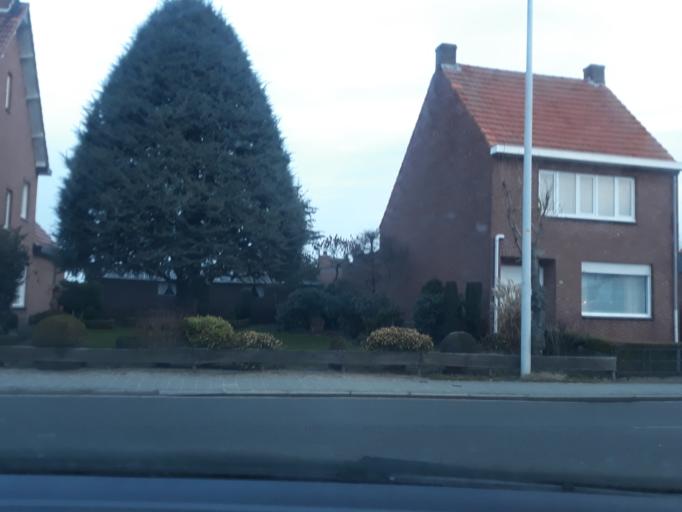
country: BE
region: Flanders
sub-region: Provincie Antwerpen
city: Ravels
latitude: 51.4098
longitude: 4.9968
